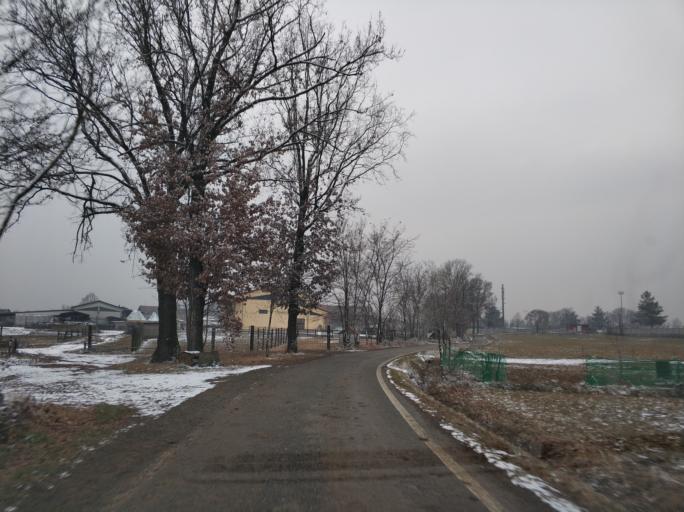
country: IT
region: Piedmont
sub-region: Provincia di Torino
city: San Francesco al Campo
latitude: 45.2344
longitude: 7.6629
